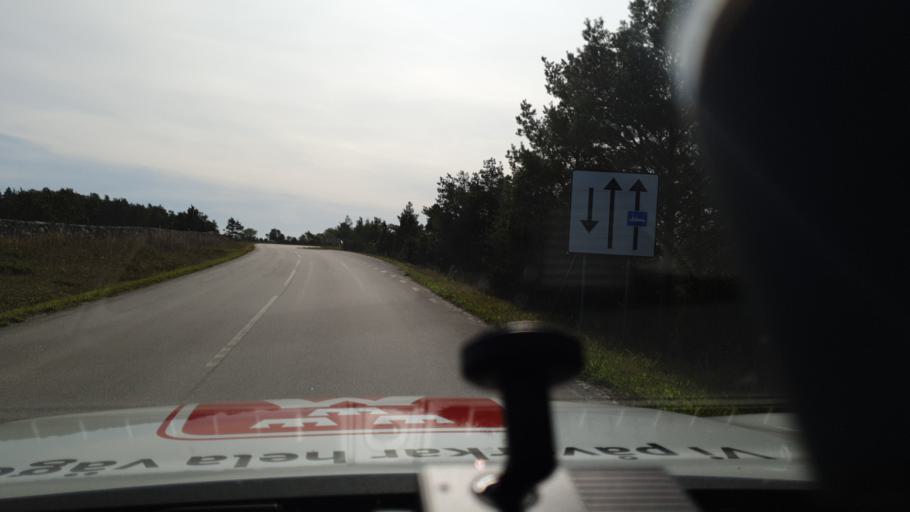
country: SE
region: Gotland
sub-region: Gotland
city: Slite
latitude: 57.8736
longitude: 19.0853
